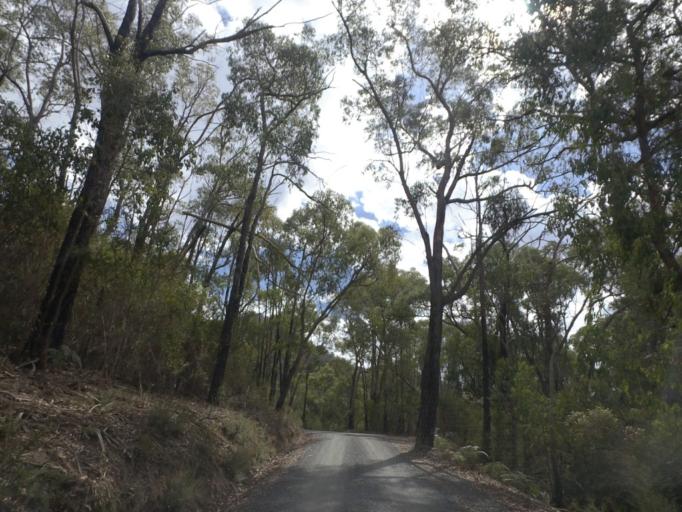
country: AU
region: Victoria
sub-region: Murrindindi
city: Alexandra
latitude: -37.3818
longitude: 145.7506
